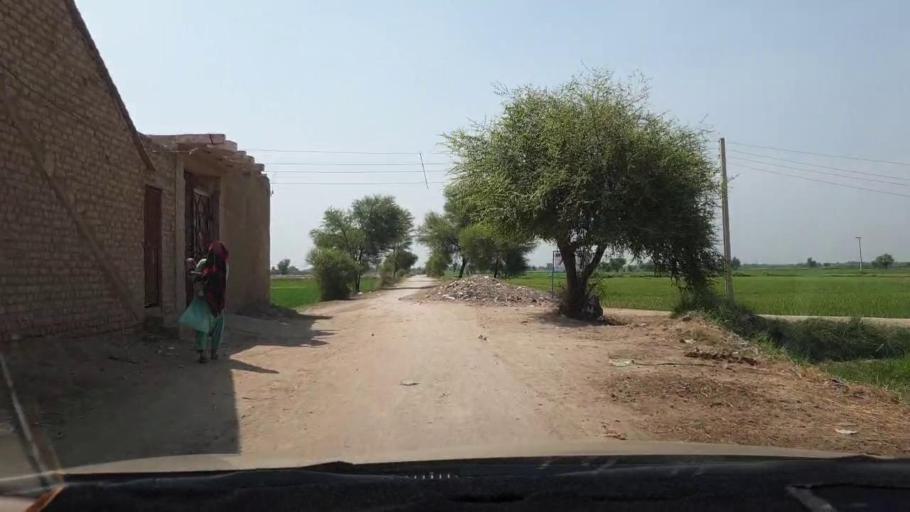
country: PK
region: Sindh
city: Naudero
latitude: 27.6385
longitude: 68.2735
